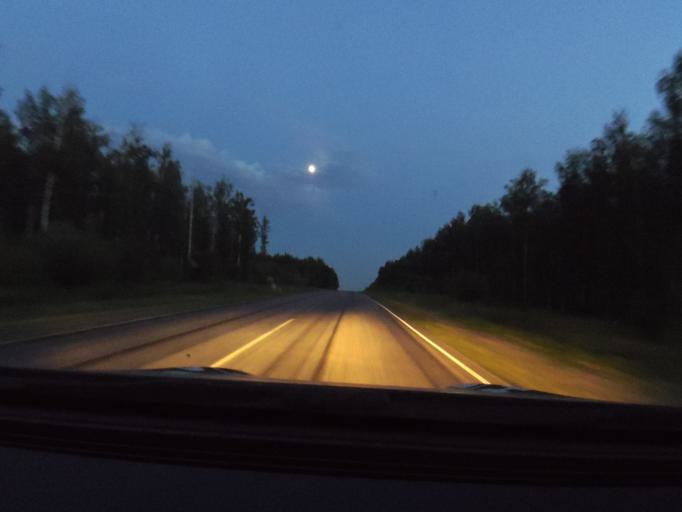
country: RU
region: Bashkortostan
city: Duvan
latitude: 55.9962
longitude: 58.2129
